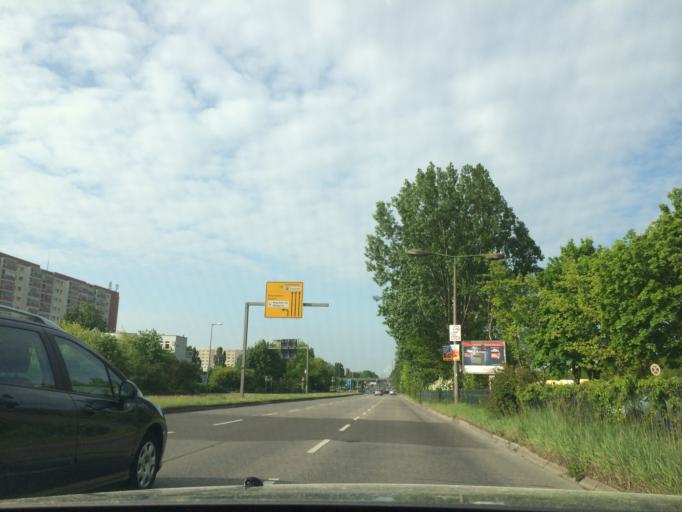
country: DE
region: Berlin
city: Falkenberg
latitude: 52.5569
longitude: 13.5534
